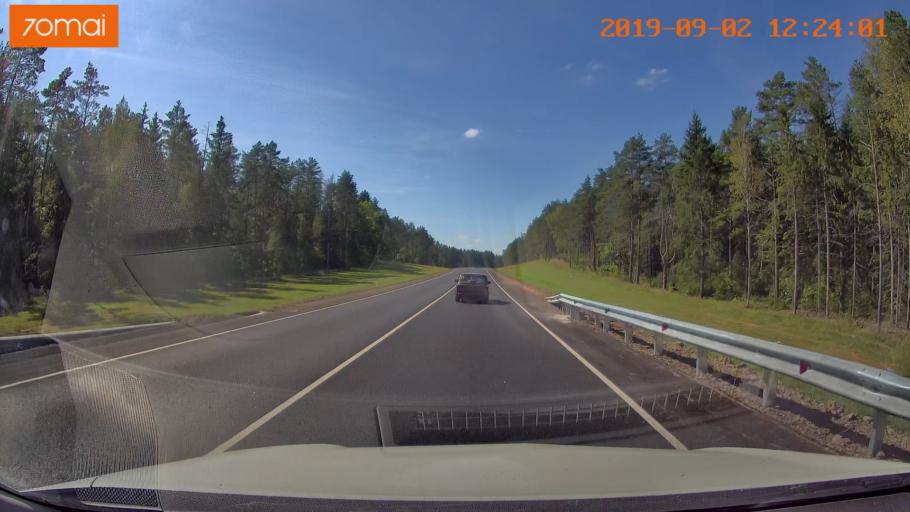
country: RU
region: Smolensk
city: Shumyachi
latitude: 53.8717
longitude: 32.6150
